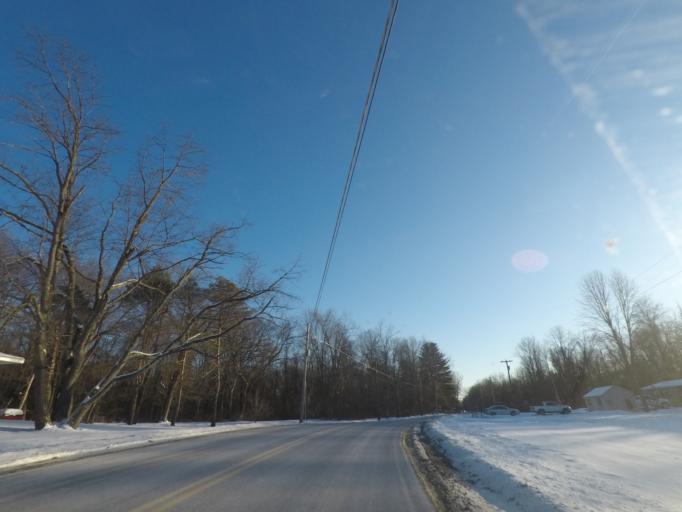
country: US
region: New York
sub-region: Saratoga County
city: Mechanicville
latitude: 42.8648
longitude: -73.6706
